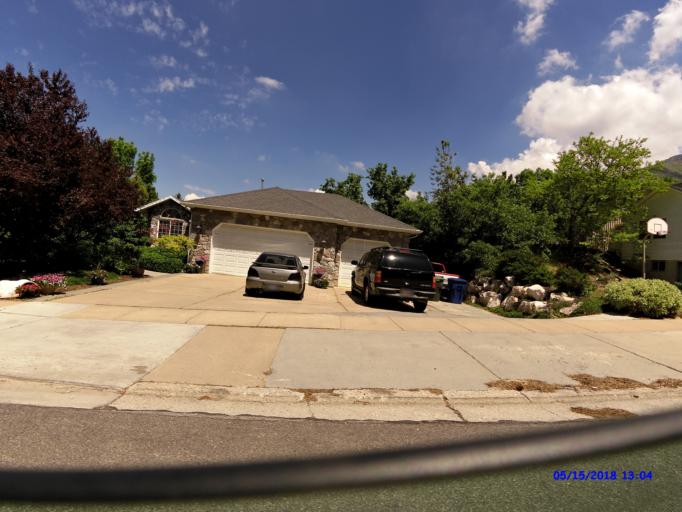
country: US
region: Utah
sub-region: Weber County
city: South Ogden
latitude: 41.1795
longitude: -111.9402
